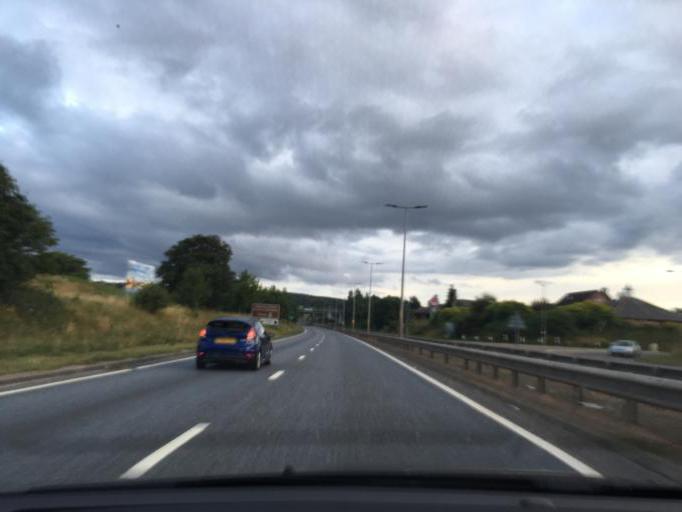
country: GB
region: Scotland
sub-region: Highland
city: Inverness
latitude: 57.4748
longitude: -4.1868
